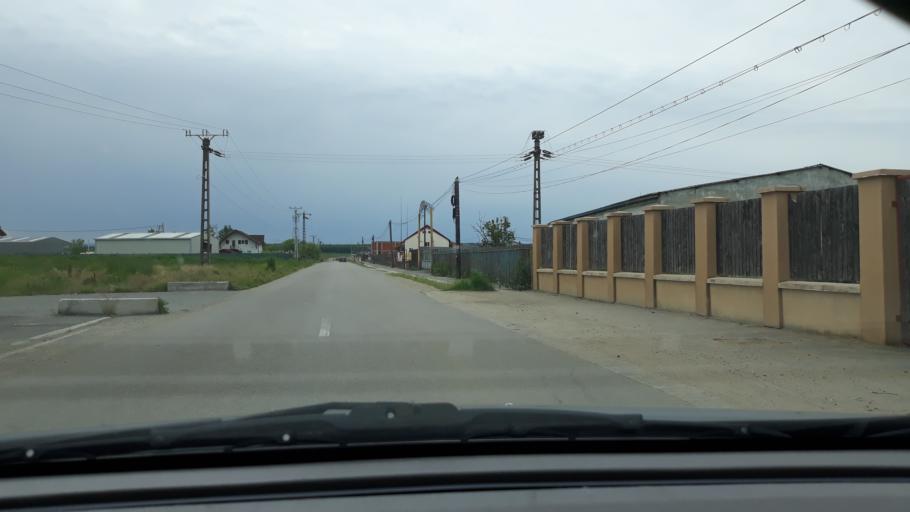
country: RO
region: Bihor
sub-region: Comuna Osorheiu
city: Osorheiu
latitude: 47.0525
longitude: 22.0455
